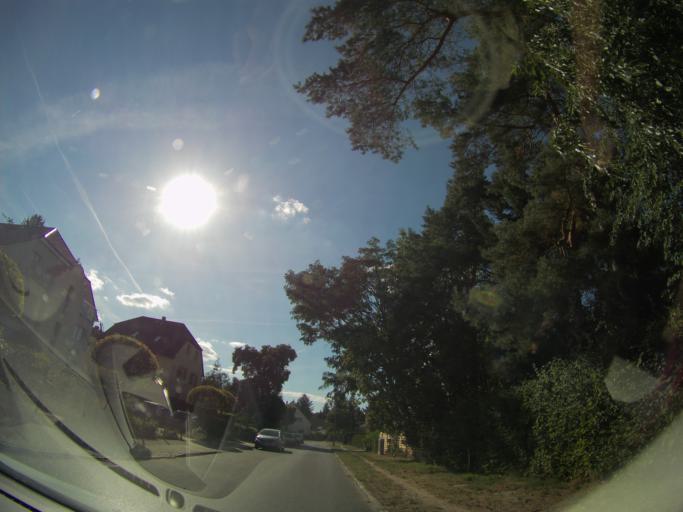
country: DE
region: Brandenburg
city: Stahnsdorf
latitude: 52.3818
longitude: 13.1969
